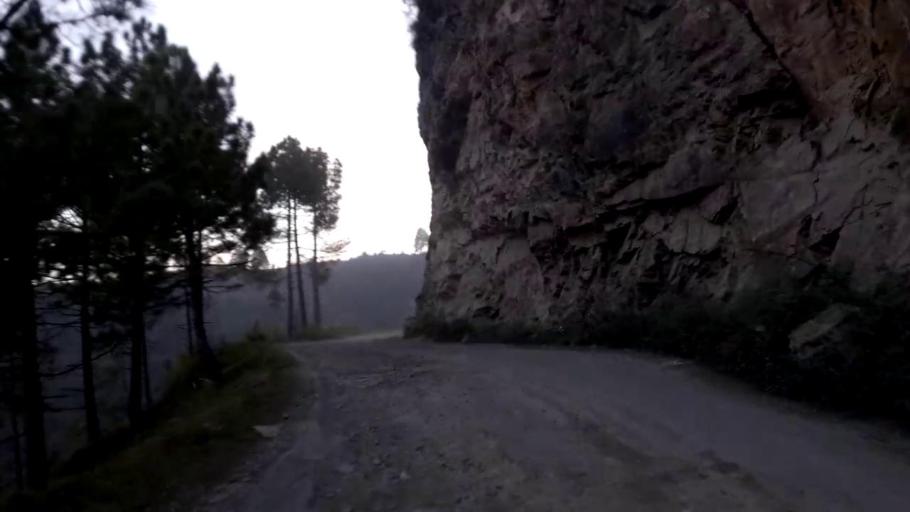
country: IN
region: Himachal Pradesh
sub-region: Shimla
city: Shimla
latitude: 31.0567
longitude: 77.1569
